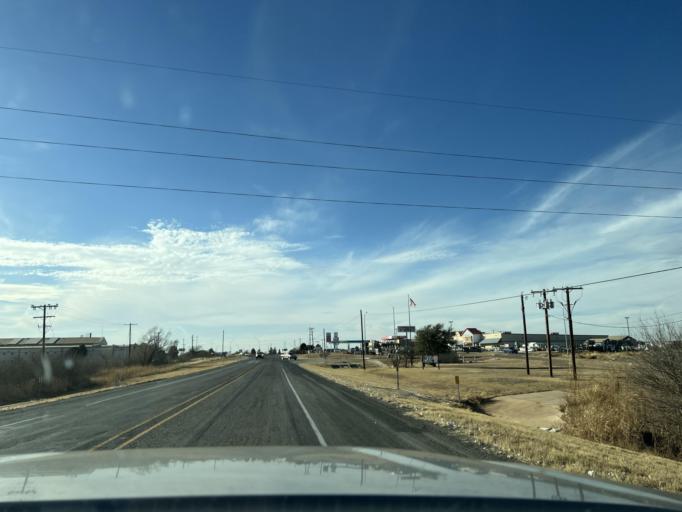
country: US
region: Texas
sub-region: Scurry County
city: Snyder
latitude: 32.7044
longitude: -100.8629
